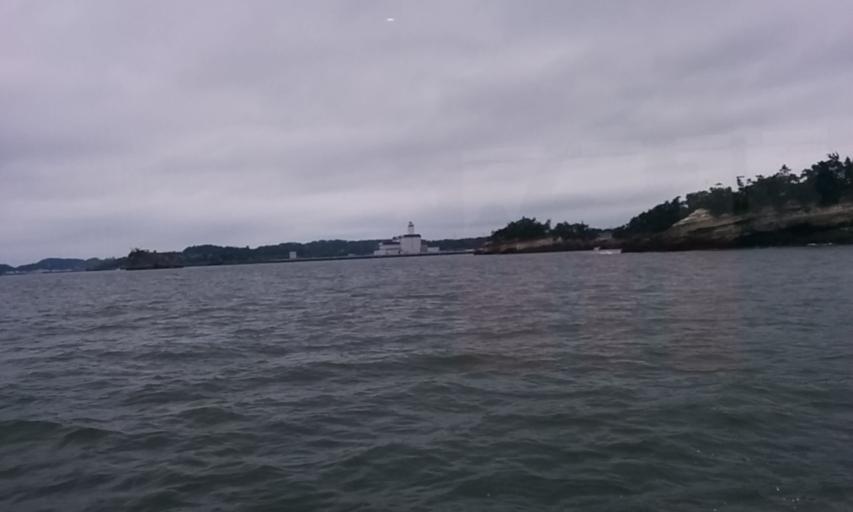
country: JP
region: Miyagi
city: Shiogama
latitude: 38.3292
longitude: 141.0776
